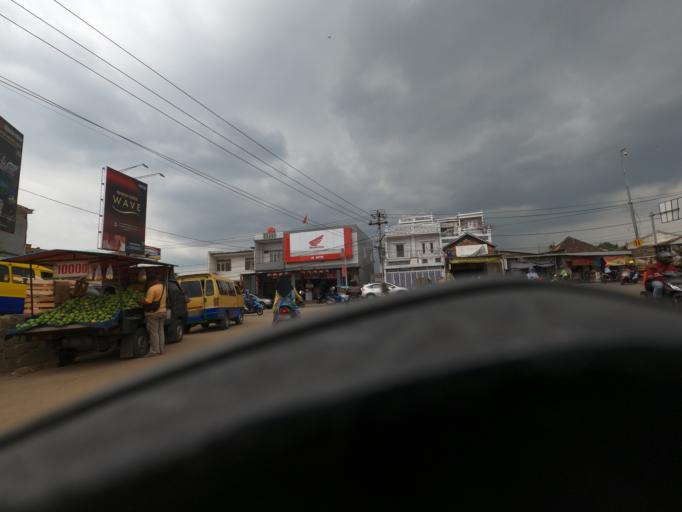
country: ID
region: West Java
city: Padalarang
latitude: -6.8445
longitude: 107.4983
